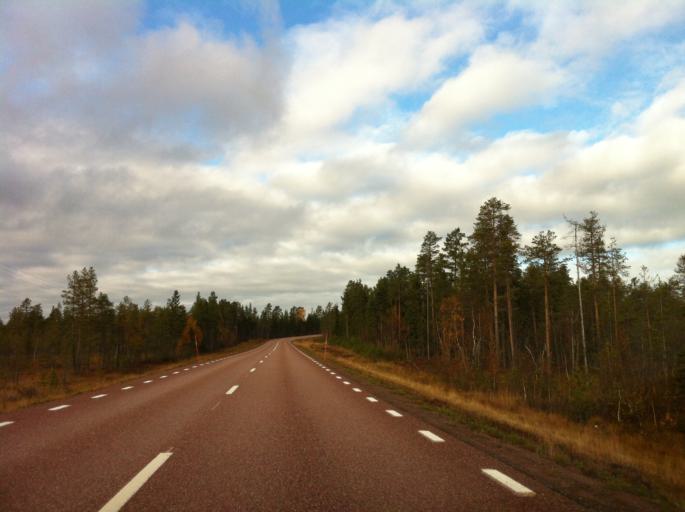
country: SE
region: Dalarna
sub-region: Alvdalens Kommun
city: AElvdalen
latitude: 61.5346
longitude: 13.3492
